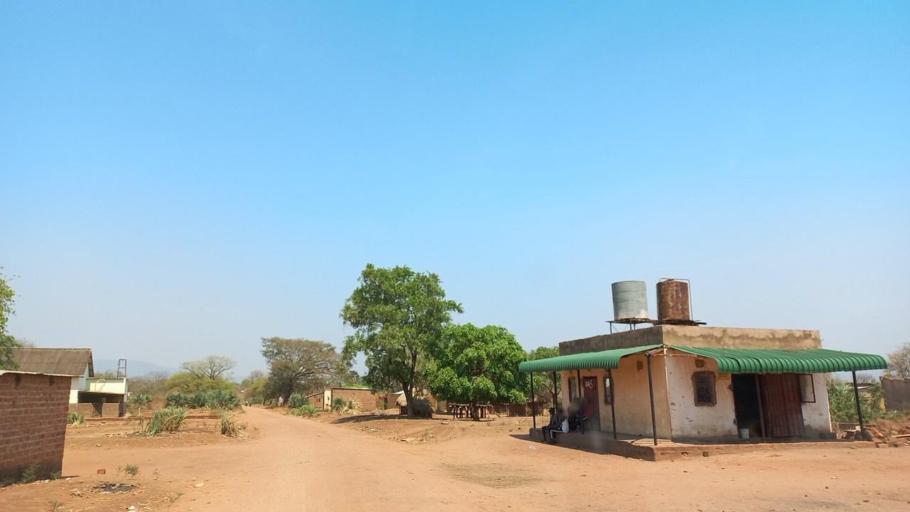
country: ZM
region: Lusaka
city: Luangwa
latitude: -15.1871
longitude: 30.2208
